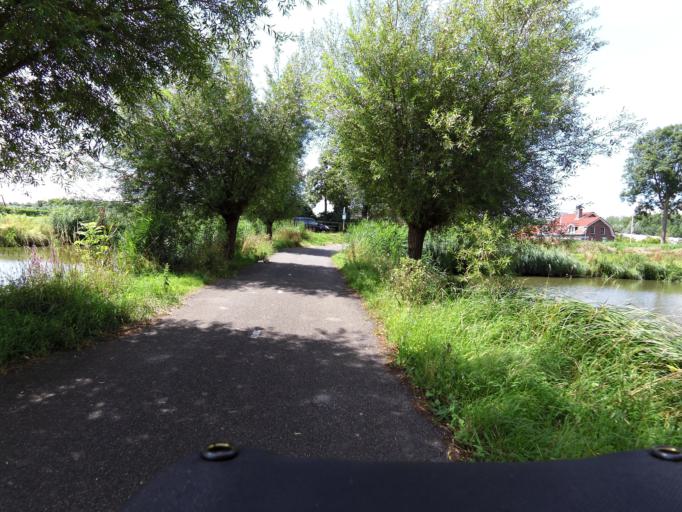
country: NL
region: South Holland
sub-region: Gemeente Albrandswaard
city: Rhoon
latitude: 51.8670
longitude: 4.4109
